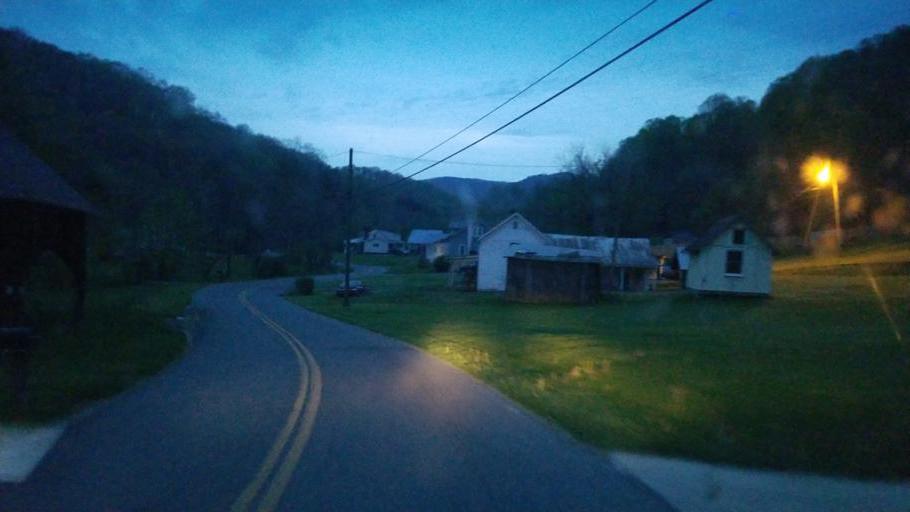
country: US
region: Virginia
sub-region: Smyth County
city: Atkins
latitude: 36.8418
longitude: -81.4617
